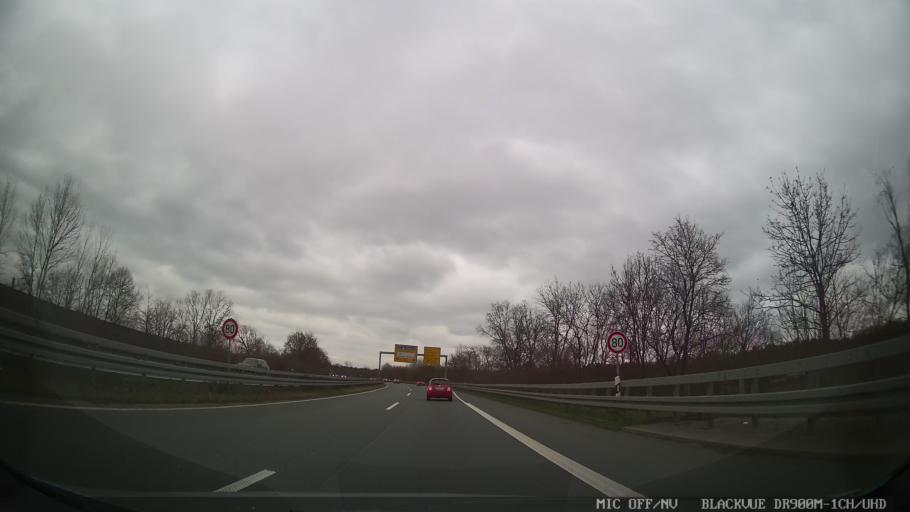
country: DE
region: Hesse
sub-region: Regierungsbezirk Darmstadt
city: Munster
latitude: 49.9087
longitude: 8.8608
